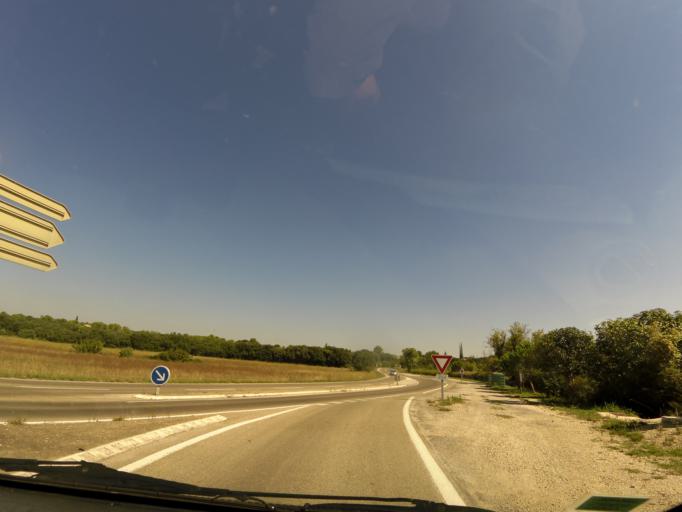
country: FR
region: Languedoc-Roussillon
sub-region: Departement du Gard
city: Villevieille
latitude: 43.7993
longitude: 4.1051
